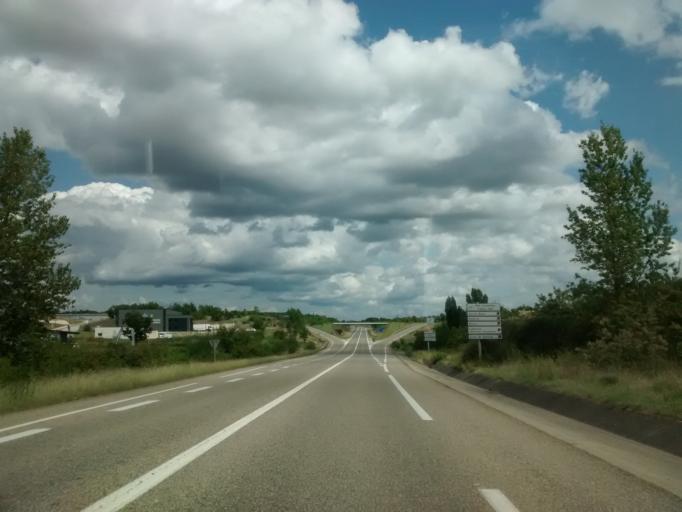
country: FR
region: Midi-Pyrenees
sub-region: Departement du Lot
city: Lalbenque
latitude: 44.3444
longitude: 1.4763
